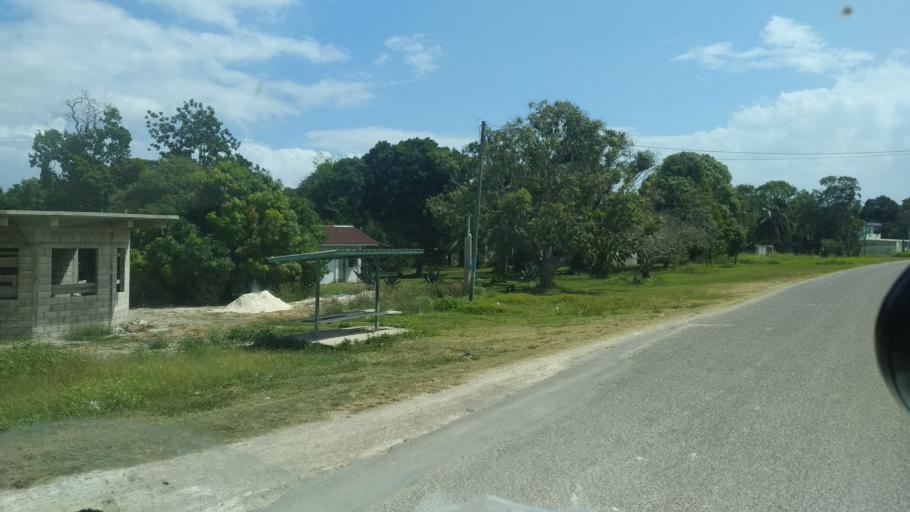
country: BZ
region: Corozal
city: Corozal
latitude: 18.3903
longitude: -88.4165
